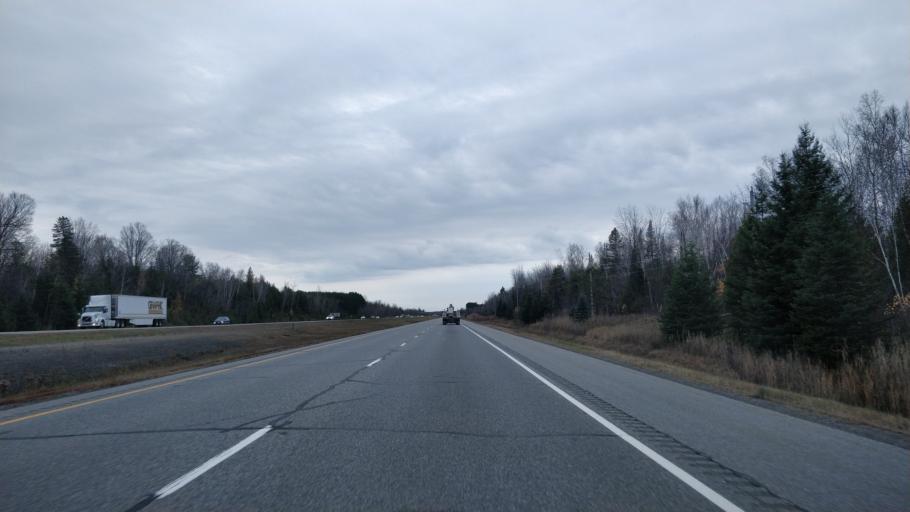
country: CA
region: Ontario
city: Bells Corners
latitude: 45.0422
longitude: -75.6243
